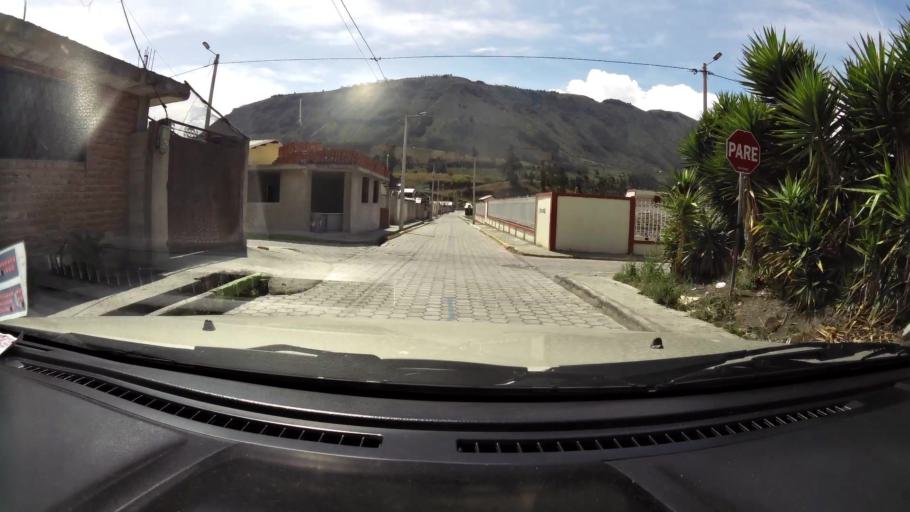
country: EC
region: Chimborazo
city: Guano
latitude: -1.5688
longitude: -78.5309
